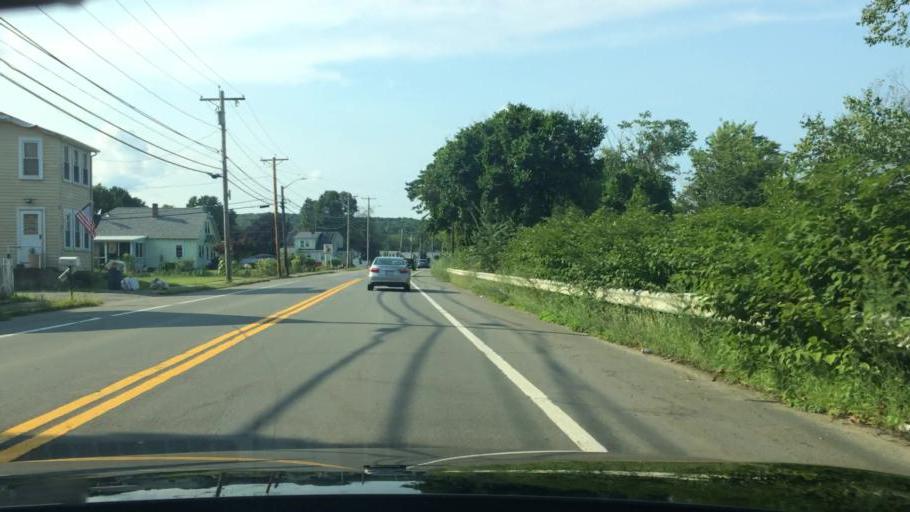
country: US
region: Massachusetts
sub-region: Essex County
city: Haverhill
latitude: 42.7563
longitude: -71.1306
